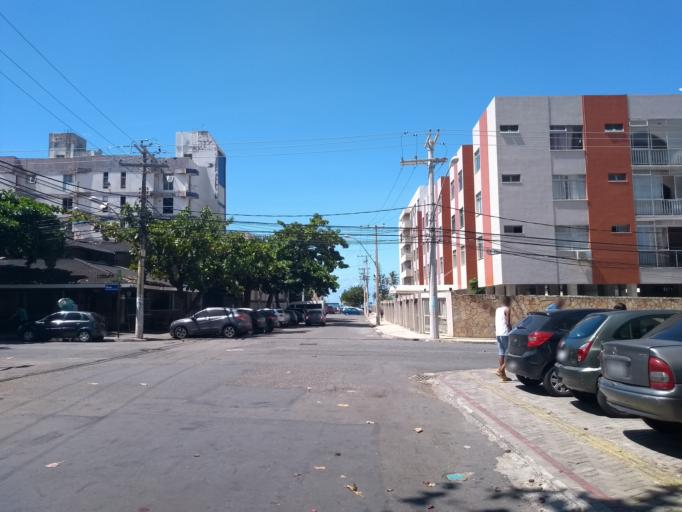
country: BR
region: Bahia
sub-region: Salvador
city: Salvador
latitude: -13.0037
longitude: -38.4570
